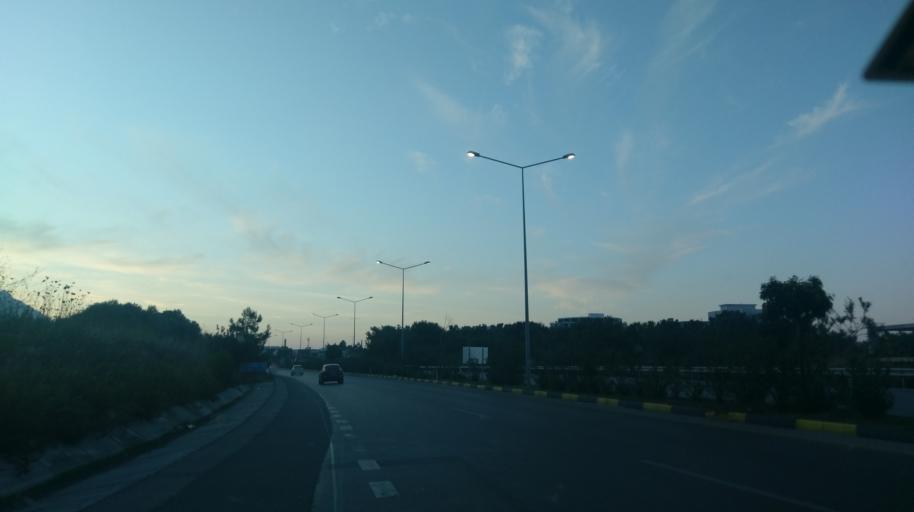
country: CY
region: Keryneia
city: Kyrenia
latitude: 35.3272
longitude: 33.3138
